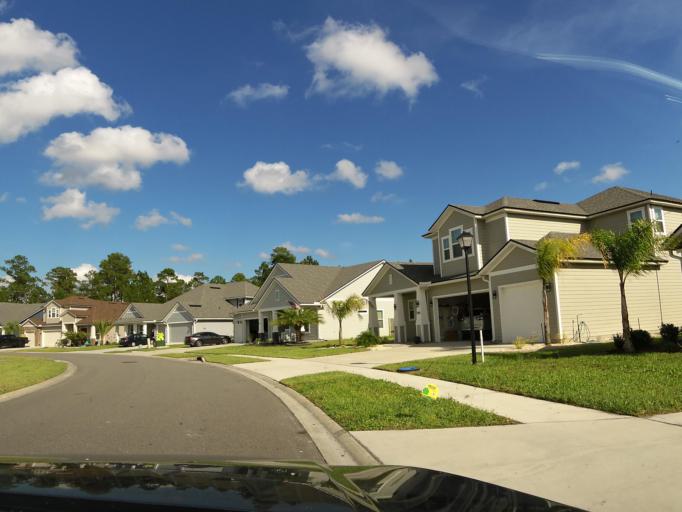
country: US
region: Florida
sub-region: Saint Johns County
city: Saint Augustine
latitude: 29.9193
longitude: -81.4933
